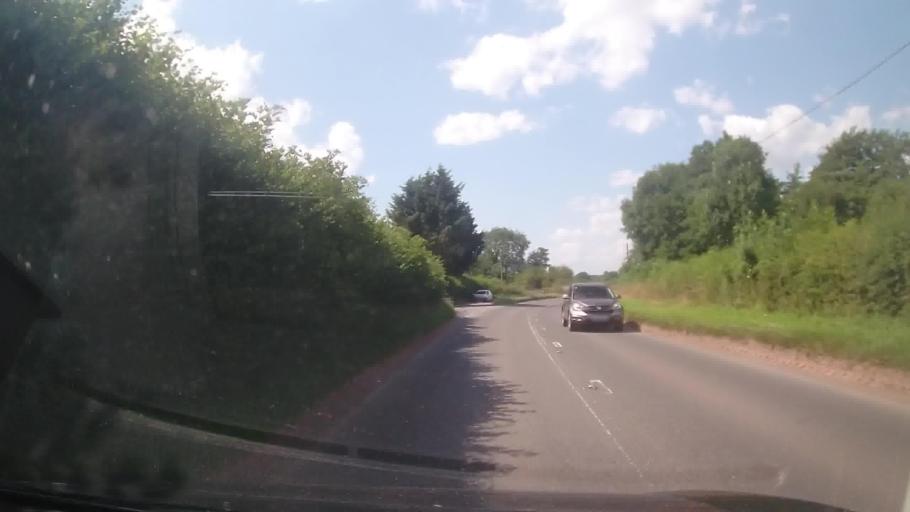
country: GB
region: England
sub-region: Herefordshire
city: Bodenham
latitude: 52.1554
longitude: -2.6557
